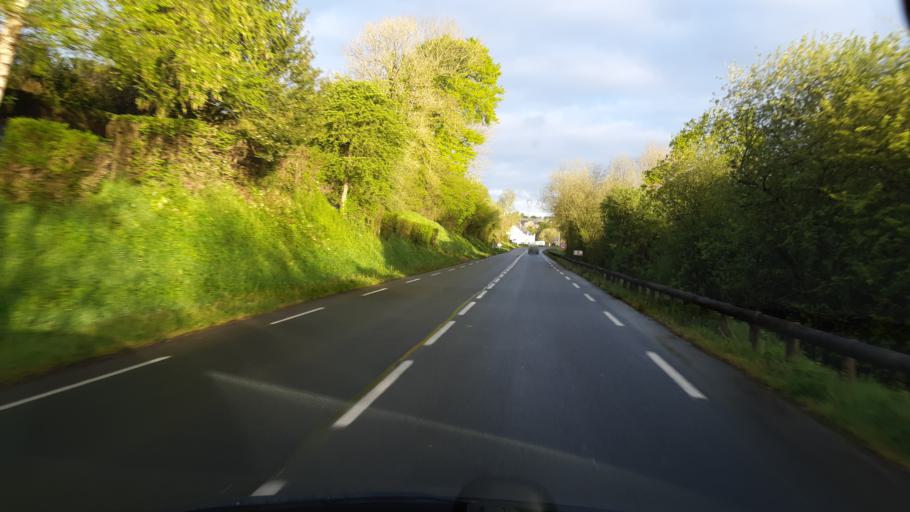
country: FR
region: Lower Normandy
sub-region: Departement de la Manche
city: Agneaux
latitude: 49.0884
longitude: -1.1160
